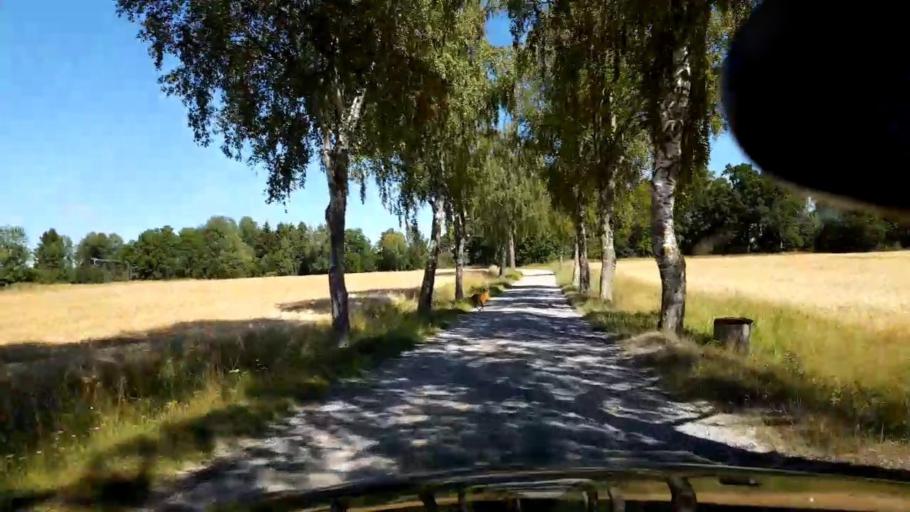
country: SE
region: Stockholm
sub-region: Sigtuna Kommun
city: Sigtuna
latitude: 59.6127
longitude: 17.6372
